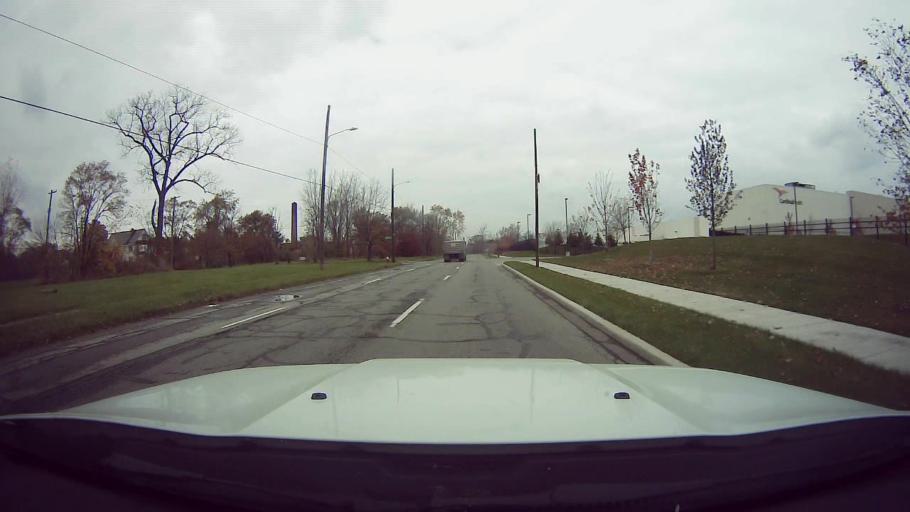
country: US
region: Michigan
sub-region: Wayne County
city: Detroit
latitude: 42.3575
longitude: -83.0867
